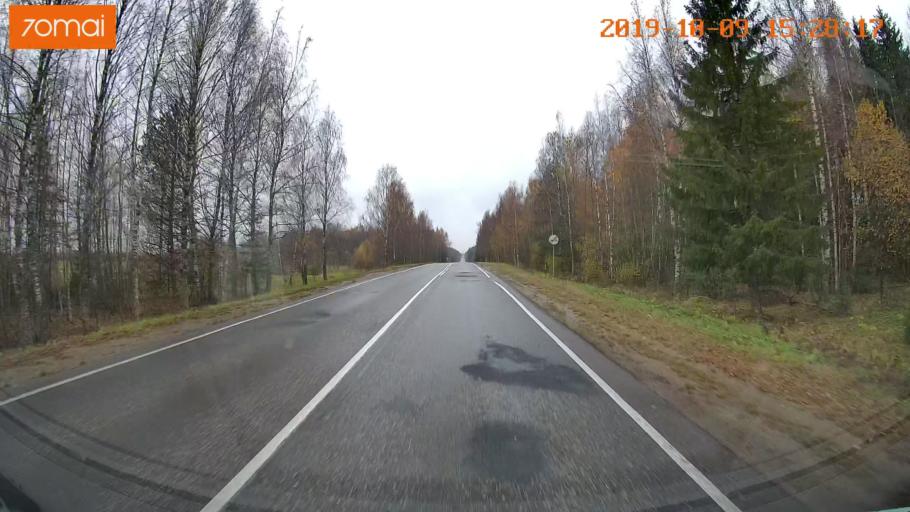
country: RU
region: Kostroma
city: Susanino
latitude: 58.0048
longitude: 41.3625
